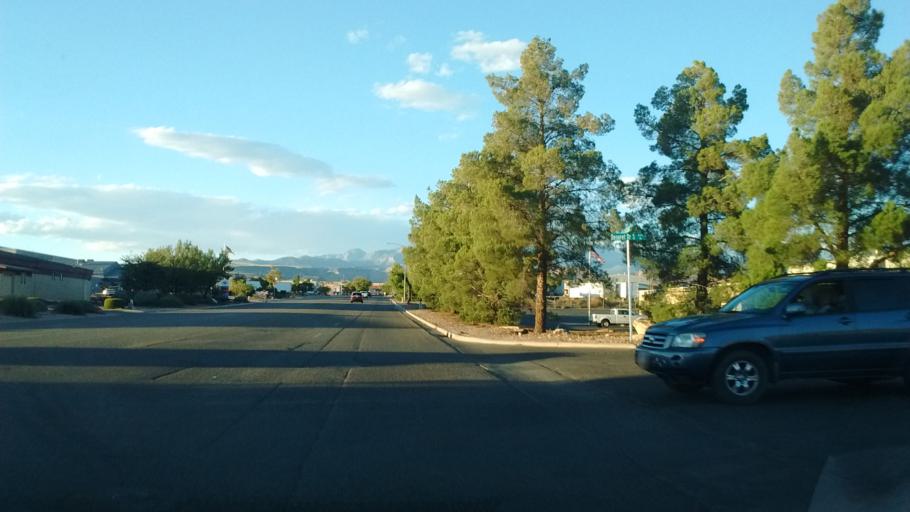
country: US
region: Utah
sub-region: Washington County
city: Washington
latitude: 37.1143
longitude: -113.5206
